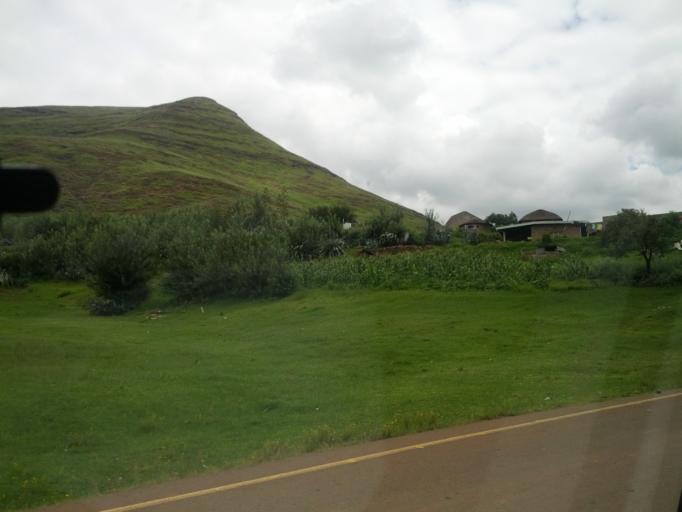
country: LS
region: Butha-Buthe
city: Butha-Buthe
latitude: -29.0329
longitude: 28.2669
